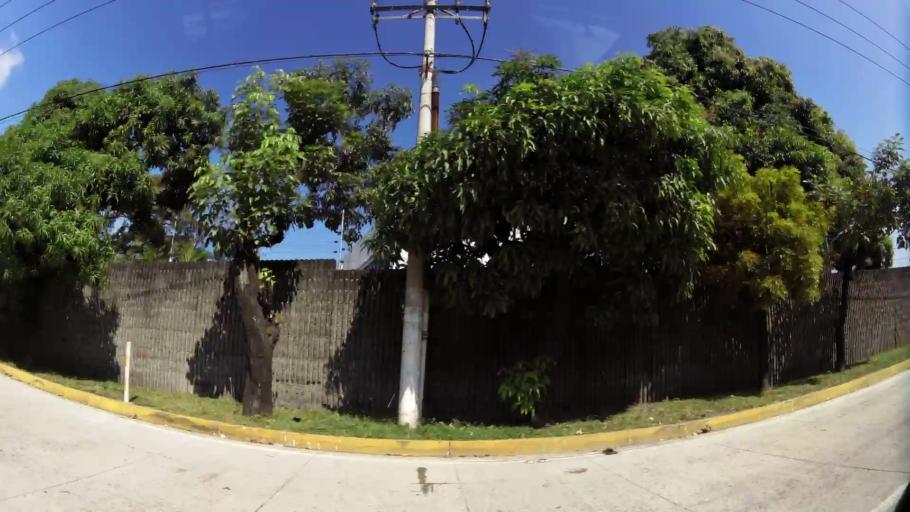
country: SV
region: La Libertad
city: Antiguo Cuscatlan
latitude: 13.6749
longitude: -89.2542
